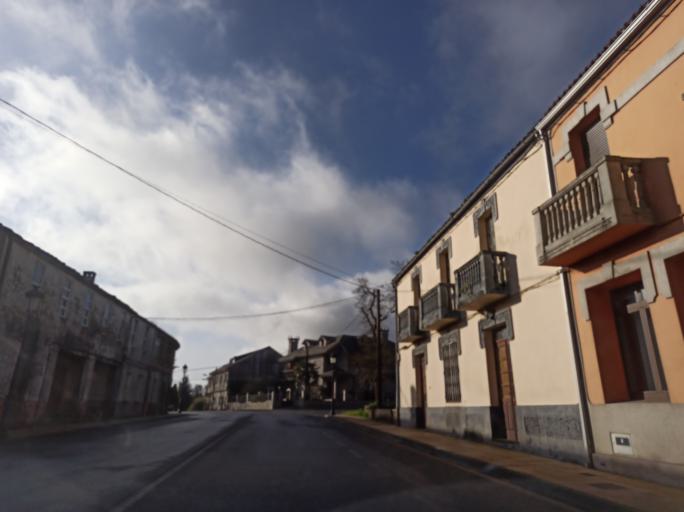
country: ES
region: Galicia
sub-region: Provincia da Coruna
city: Sobrado
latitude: 43.0787
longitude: -8.0132
